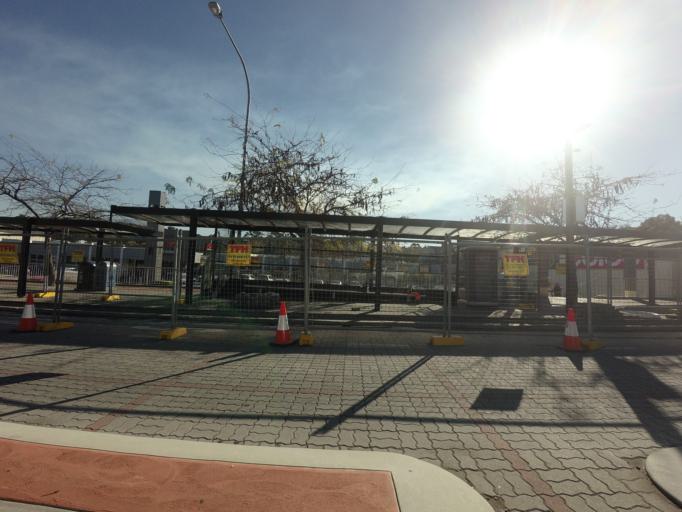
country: AU
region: Tasmania
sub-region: Clarence
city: Bellerive
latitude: -42.8658
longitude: 147.3695
